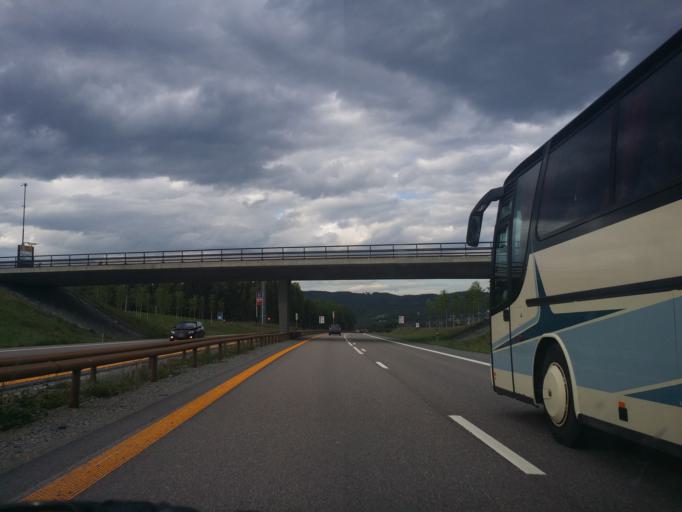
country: NO
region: Akershus
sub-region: Eidsvoll
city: Eidsvoll
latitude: 60.3893
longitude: 11.2155
